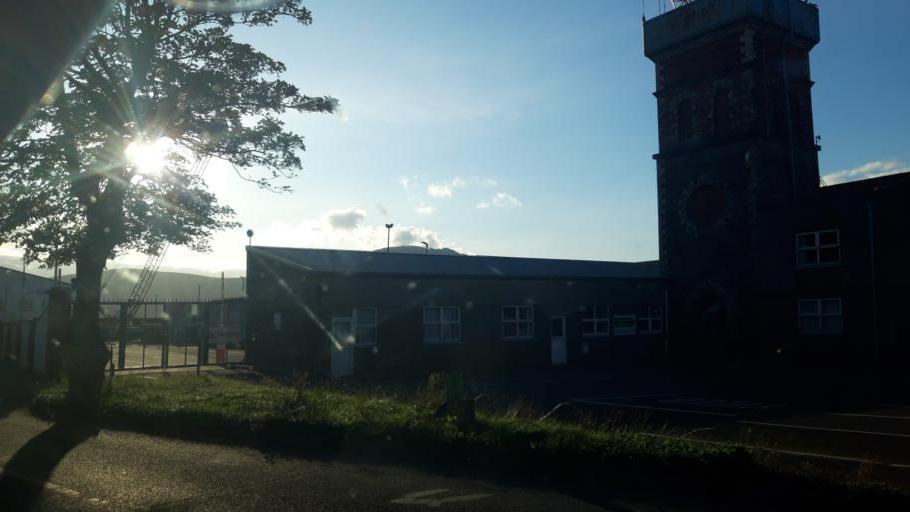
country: IE
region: Leinster
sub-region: Lu
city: Carlingford
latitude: 54.0326
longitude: -6.1335
